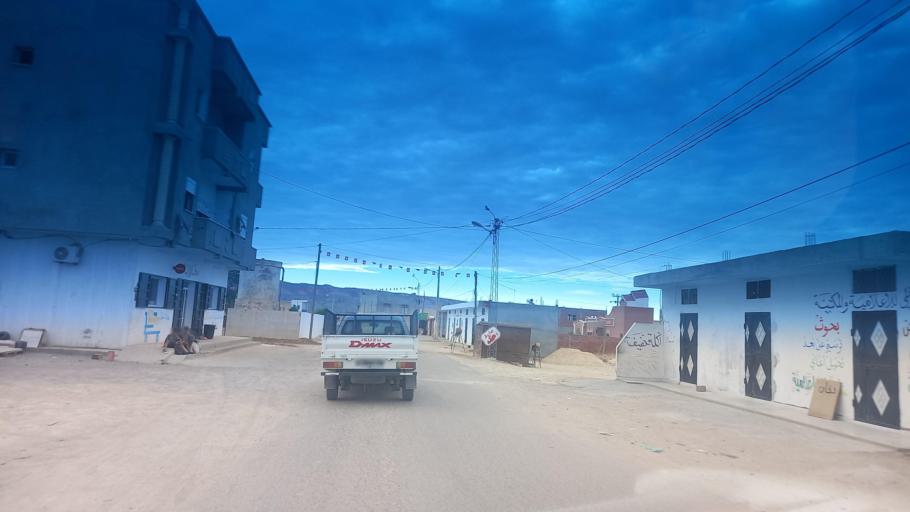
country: TN
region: Al Qasrayn
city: Sbiba
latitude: 35.3622
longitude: 9.0906
